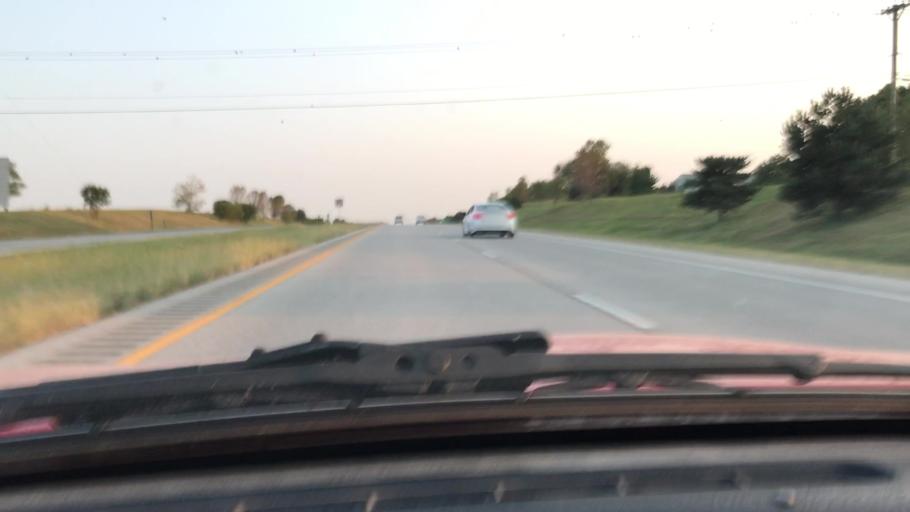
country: US
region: Nebraska
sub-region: Lancaster County
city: Lincoln
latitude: 40.7778
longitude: -96.7274
